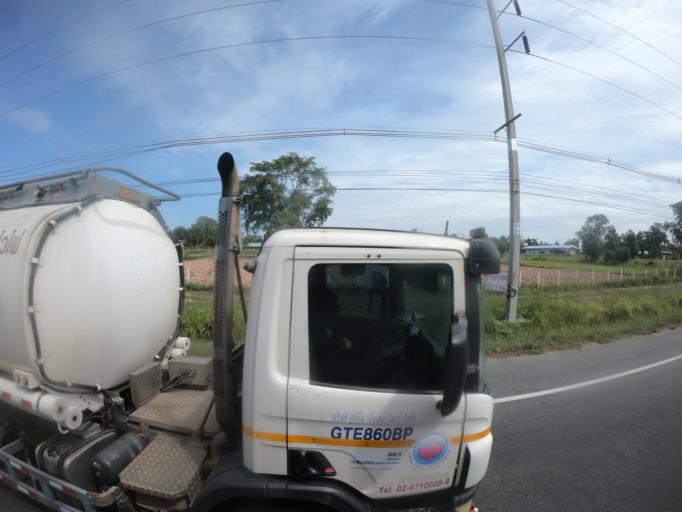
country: TH
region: Maha Sarakham
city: Chiang Yuen
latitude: 16.4329
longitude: 103.0569
